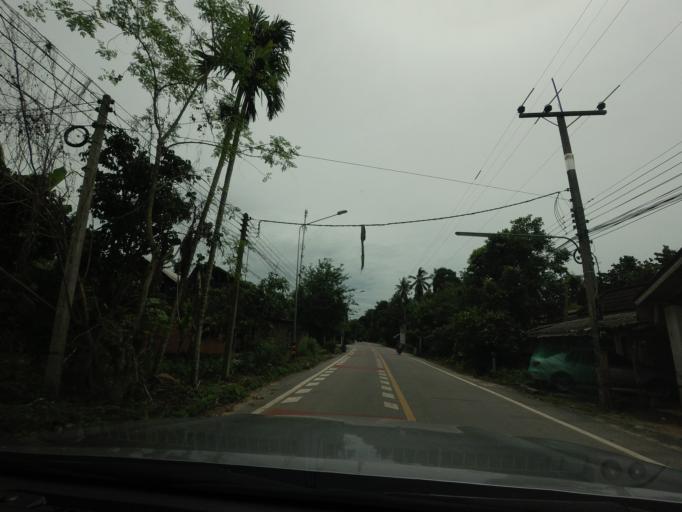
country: TH
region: Pattani
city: Kapho
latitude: 6.5957
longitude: 101.5303
